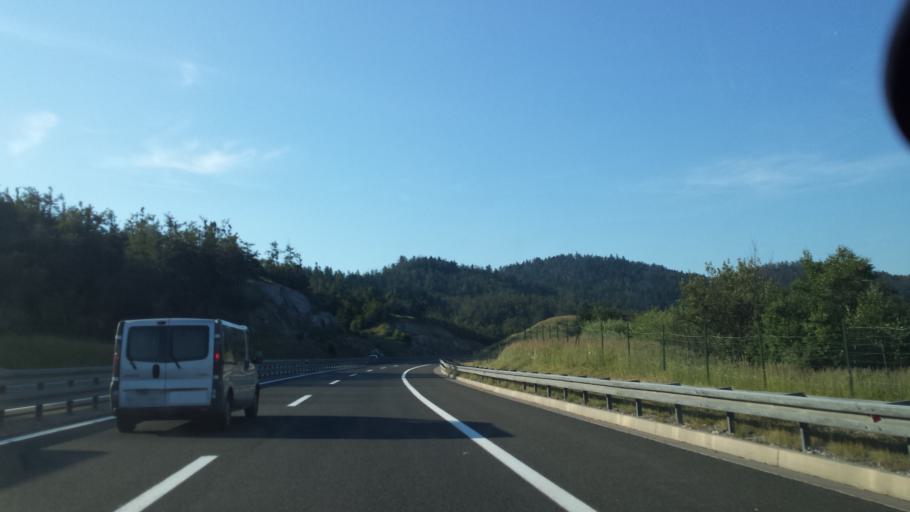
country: HR
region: Primorsko-Goranska
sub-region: Grad Delnice
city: Delnice
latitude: 45.3313
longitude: 14.7386
